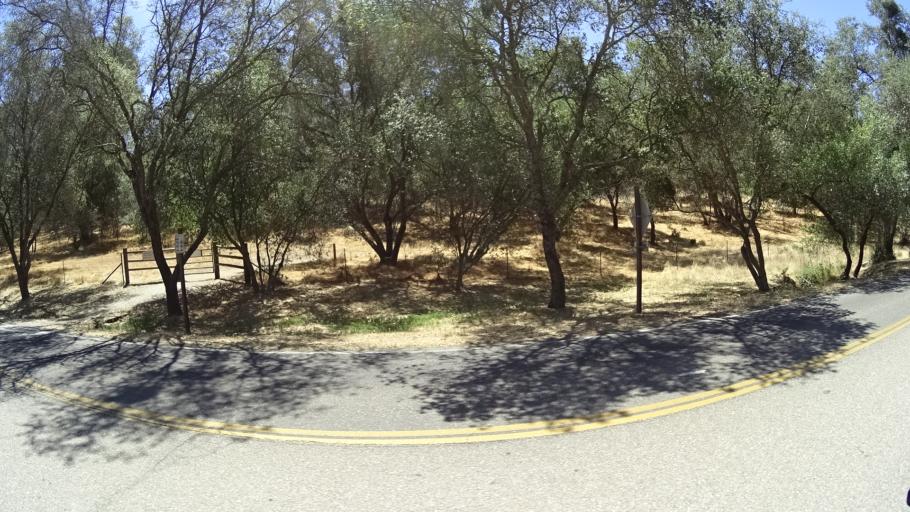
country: US
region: California
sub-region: Calaveras County
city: Valley Springs
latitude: 38.2115
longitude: -120.9150
